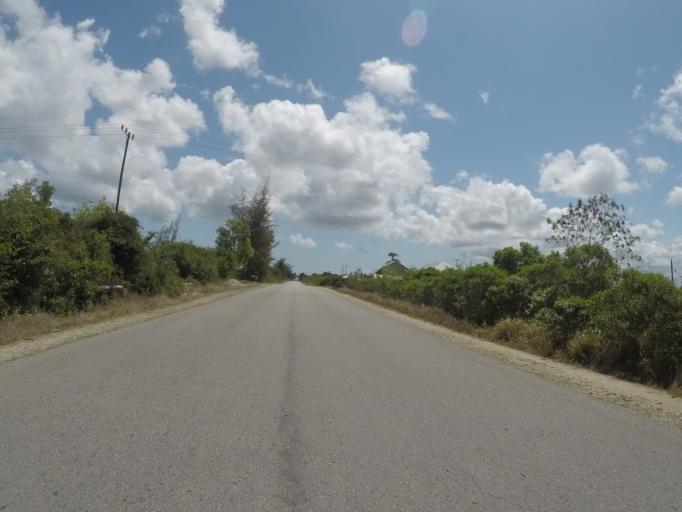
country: TZ
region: Zanzibar Central/South
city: Nganane
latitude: -6.2824
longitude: 39.4703
